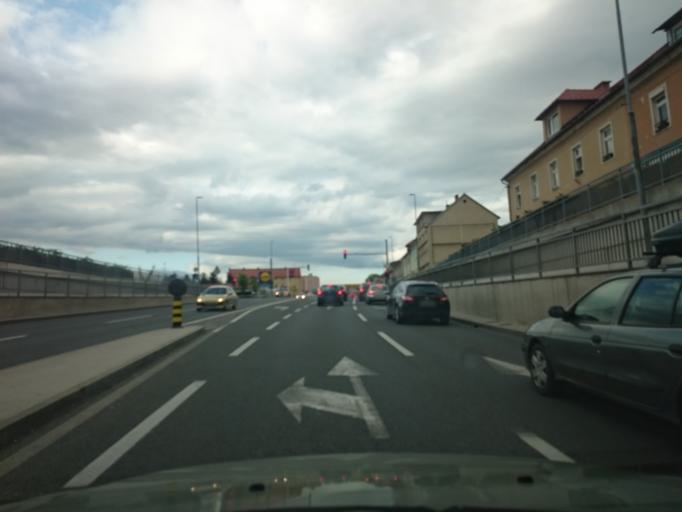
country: SI
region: Celje
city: Celje
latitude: 46.2342
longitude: 15.2690
